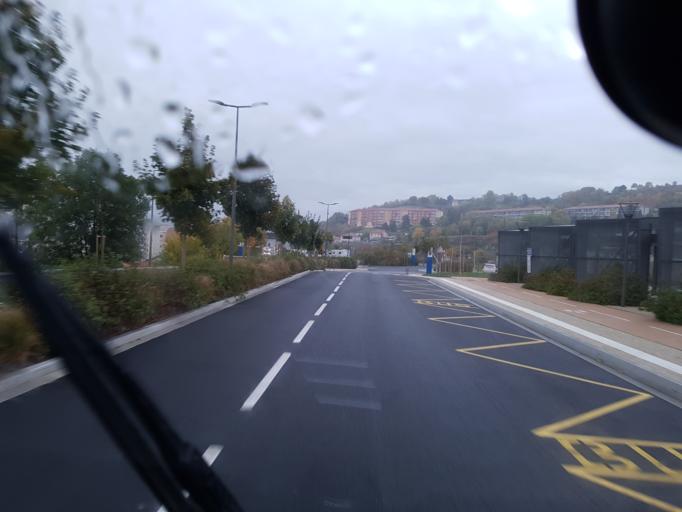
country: FR
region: Auvergne
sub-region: Departement de la Haute-Loire
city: Le Puy-en-Velay
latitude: 45.0442
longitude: 3.8939
